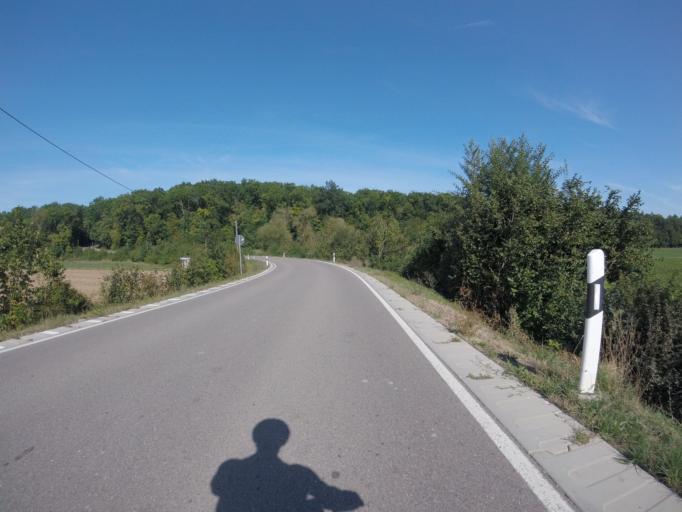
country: DE
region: Baden-Wuerttemberg
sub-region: Regierungsbezirk Stuttgart
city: Ilsfeld
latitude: 49.0369
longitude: 9.2390
